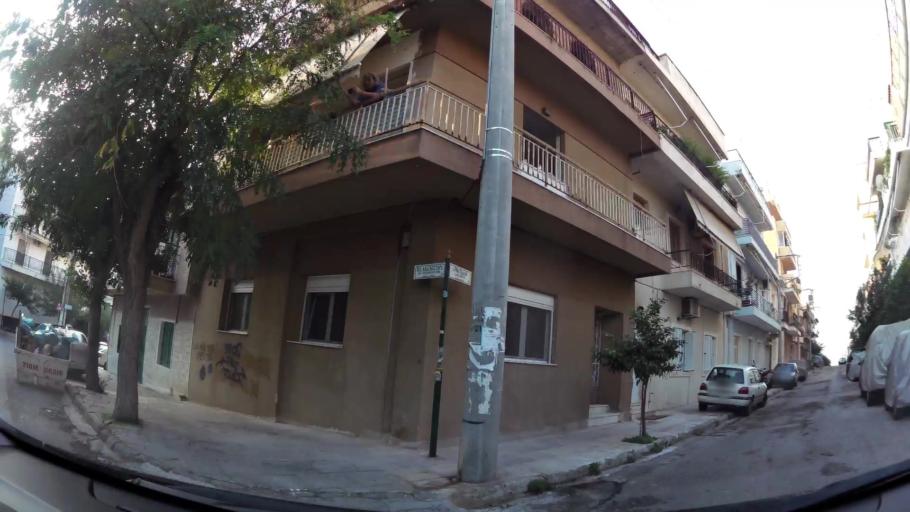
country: GR
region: Attica
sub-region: Nomarchia Athinas
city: Ymittos
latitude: 37.9488
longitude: 23.7546
